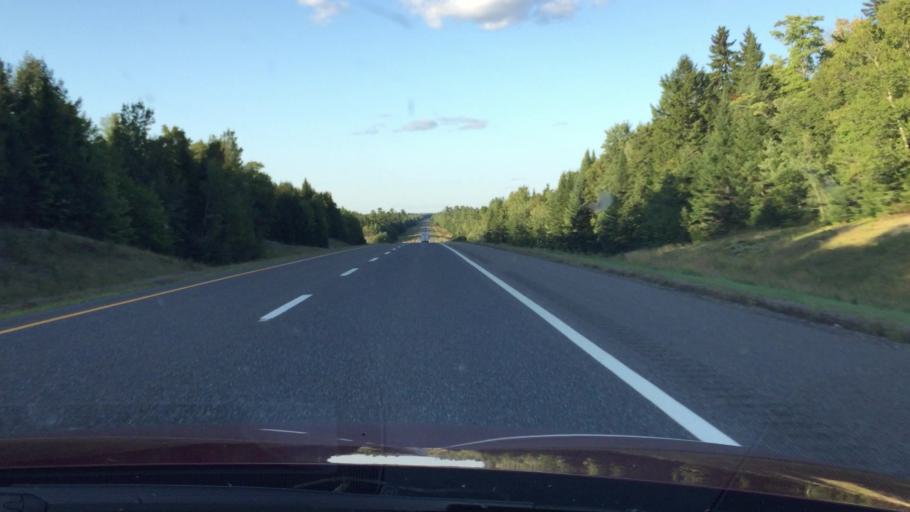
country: US
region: Maine
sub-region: Penobscot County
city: Patten
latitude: 46.0606
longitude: -68.2329
